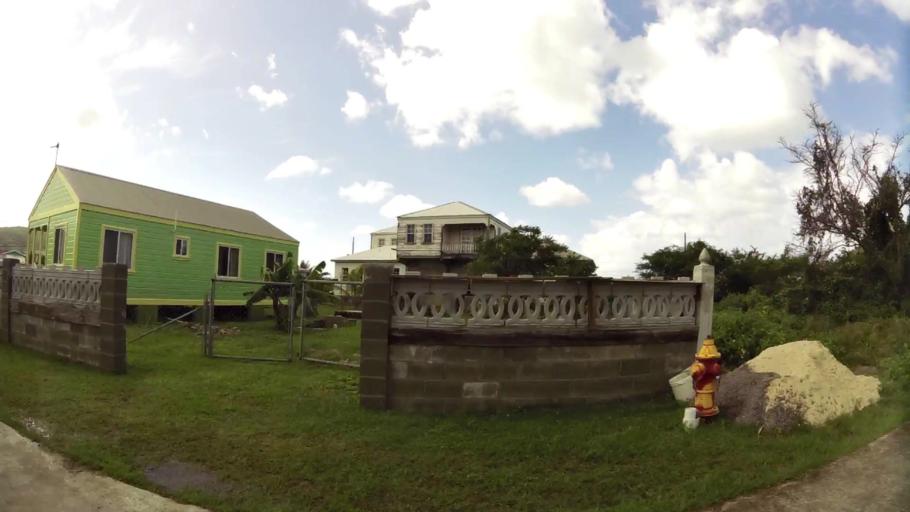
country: AG
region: Saint Mary
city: Bolands
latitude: 17.0759
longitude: -61.8748
